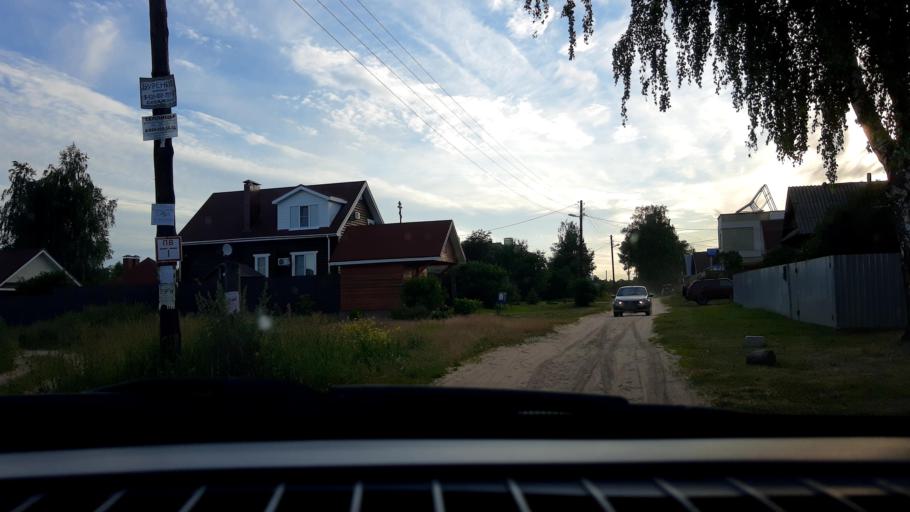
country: RU
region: Nizjnij Novgorod
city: Kstovo
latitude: 56.2646
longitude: 44.3010
